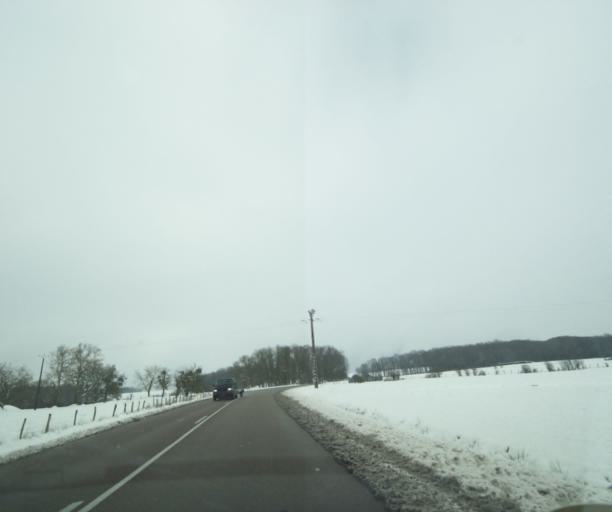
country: FR
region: Champagne-Ardenne
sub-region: Departement de la Haute-Marne
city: Montier-en-Der
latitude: 48.4473
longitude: 4.7360
